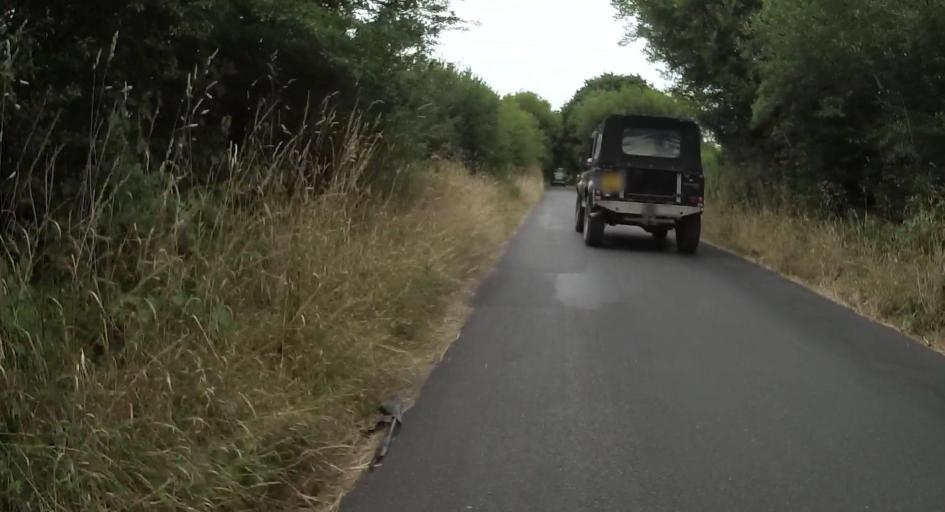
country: GB
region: England
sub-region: Dorset
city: Wareham
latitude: 50.6748
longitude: -2.0988
